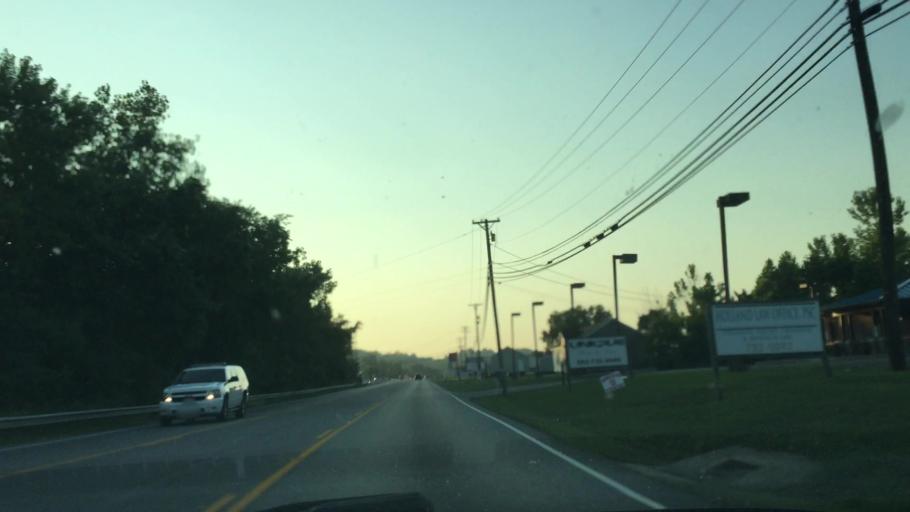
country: US
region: Kentucky
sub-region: Carroll County
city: Carrollton
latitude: 38.6591
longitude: -85.1369
